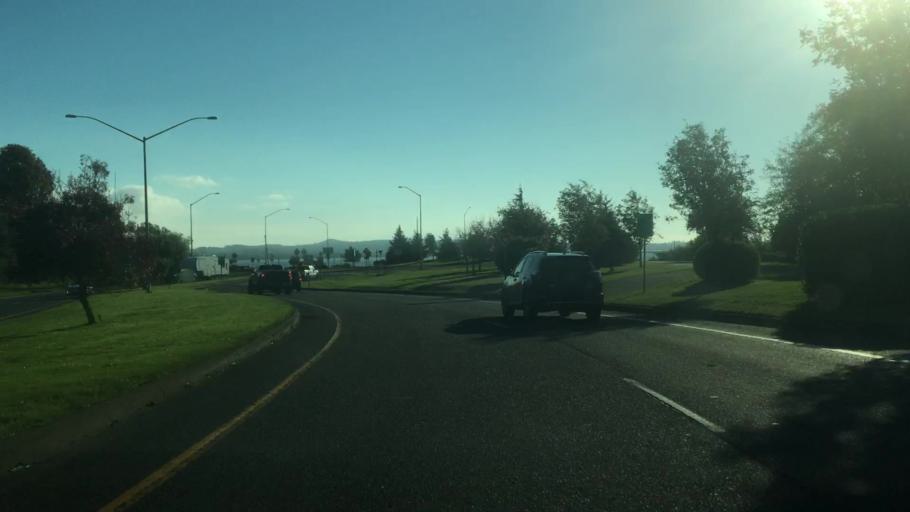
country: US
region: Oregon
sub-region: Clatsop County
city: Astoria
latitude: 46.1843
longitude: -123.8596
